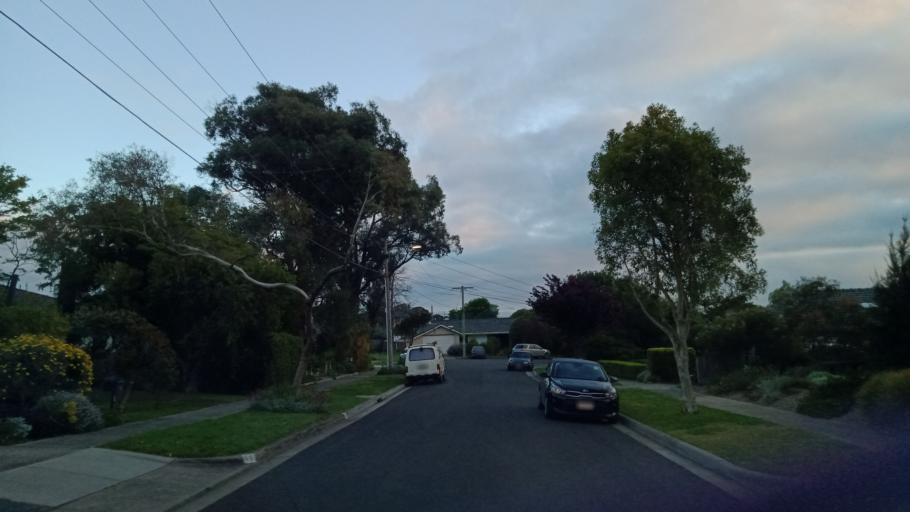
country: AU
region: Victoria
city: Burwood East
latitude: -37.8728
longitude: 145.1410
